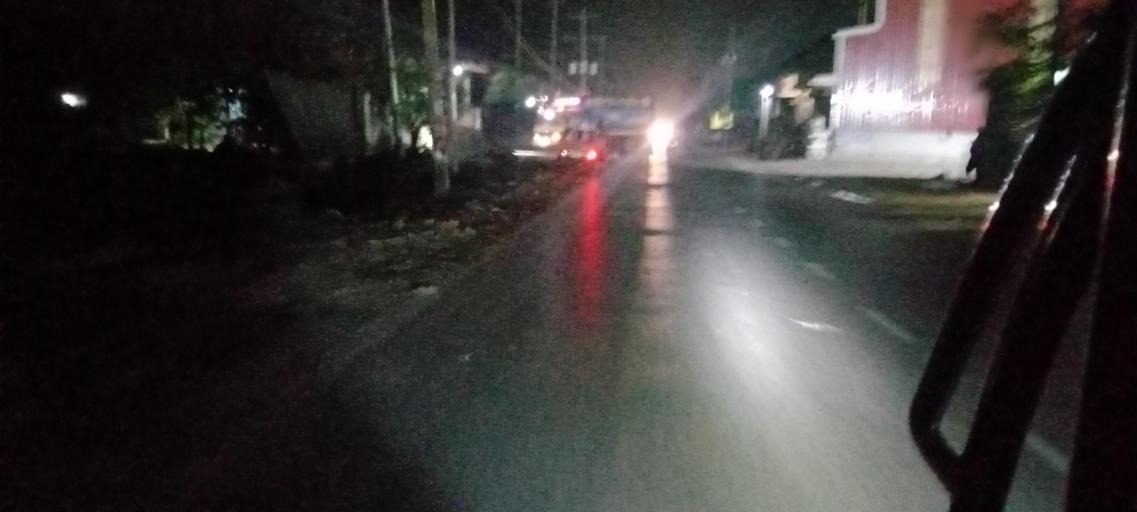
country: BD
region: Dhaka
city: Azimpur
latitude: 23.6997
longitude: 90.3633
